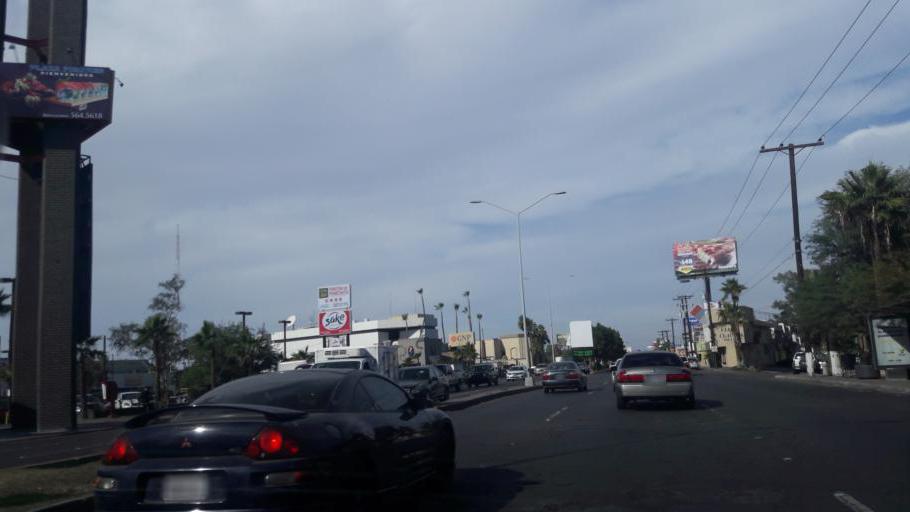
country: MX
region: Baja California
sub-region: Mexicali
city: Mexicali
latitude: 32.6412
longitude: -115.4499
